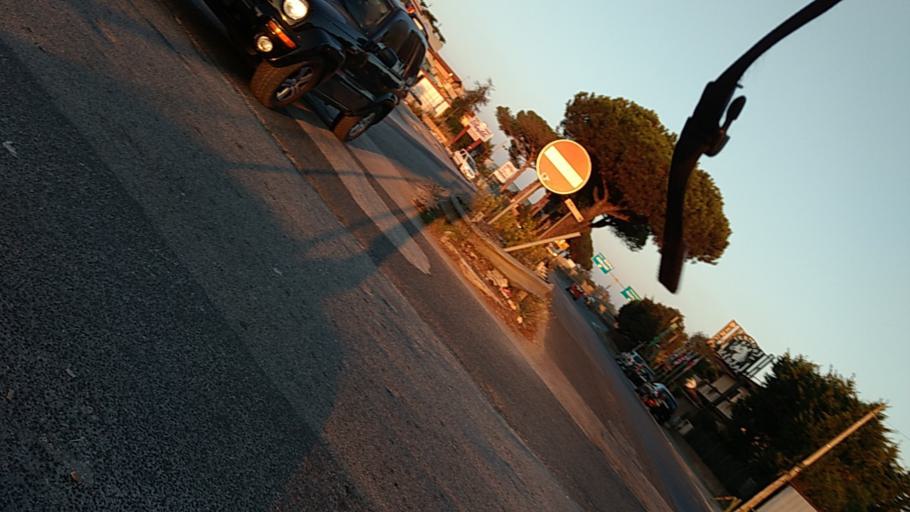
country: IT
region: Campania
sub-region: Provincia di Napoli
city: Masseria Vecchia Ovest
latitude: 40.9343
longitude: 14.0466
